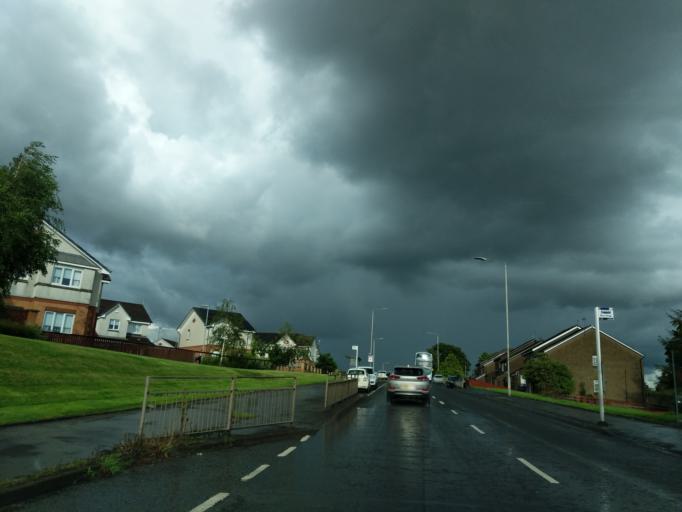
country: GB
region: Scotland
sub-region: East Renfrewshire
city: Barrhead
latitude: 55.8073
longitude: -4.3609
